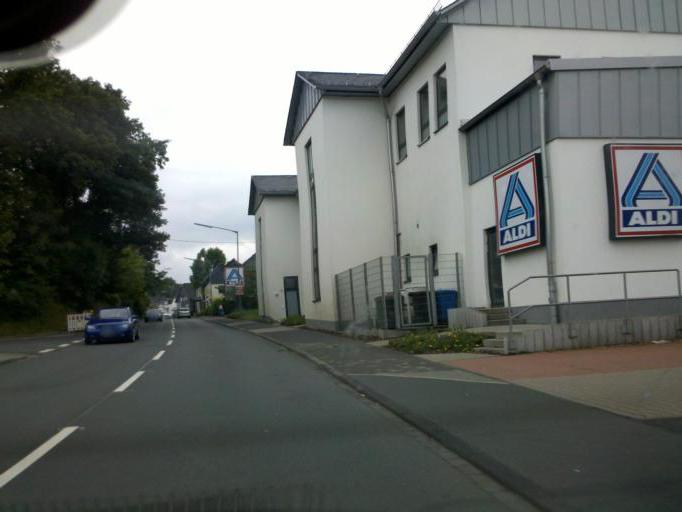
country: DE
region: North Rhine-Westphalia
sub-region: Regierungsbezirk Arnsberg
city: Wilnsdorf
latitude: 50.8175
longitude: 8.1061
